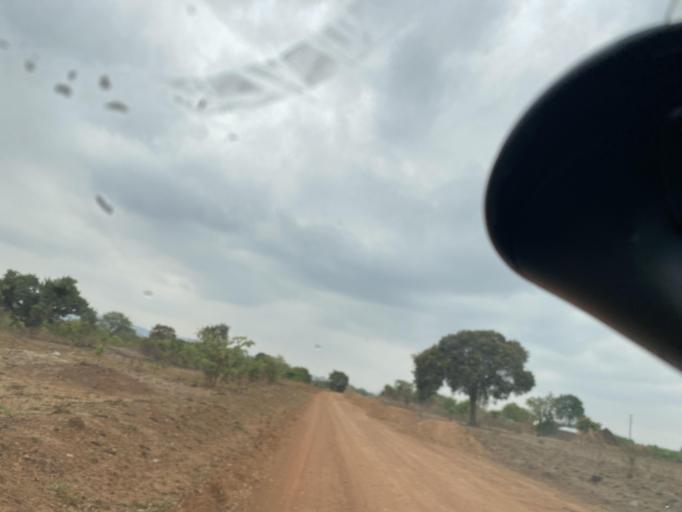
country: ZM
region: Lusaka
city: Chongwe
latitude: -15.2358
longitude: 28.7195
